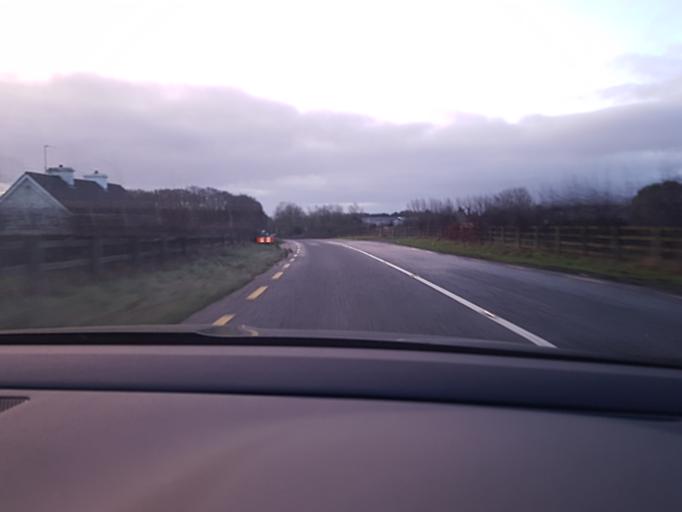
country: IE
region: Connaught
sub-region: County Galway
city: Tuam
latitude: 53.5339
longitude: -8.8792
